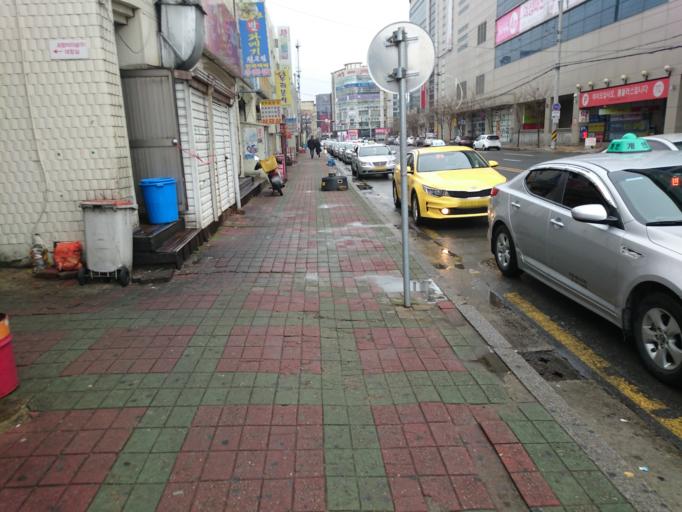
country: KR
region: Gyeongsangbuk-do
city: Enjitsu
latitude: 36.0135
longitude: 129.3486
